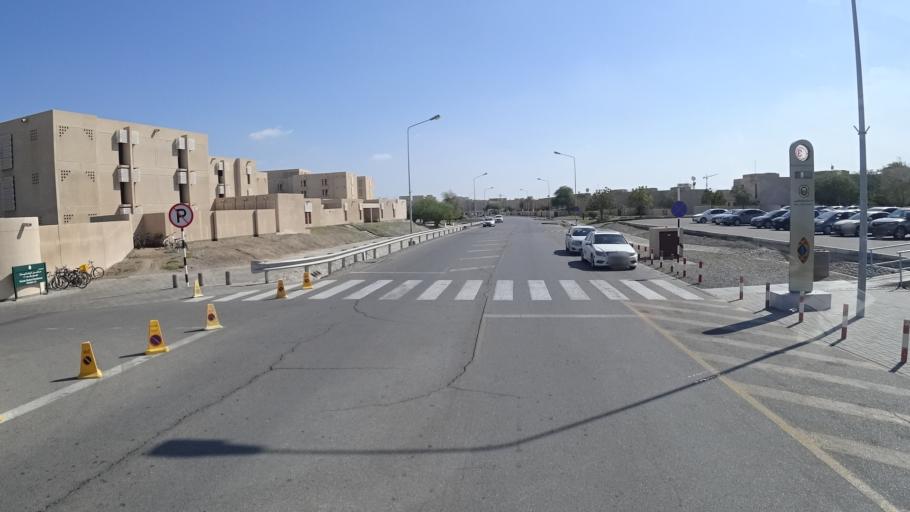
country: OM
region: Muhafazat Masqat
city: As Sib al Jadidah
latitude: 23.5860
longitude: 58.1660
